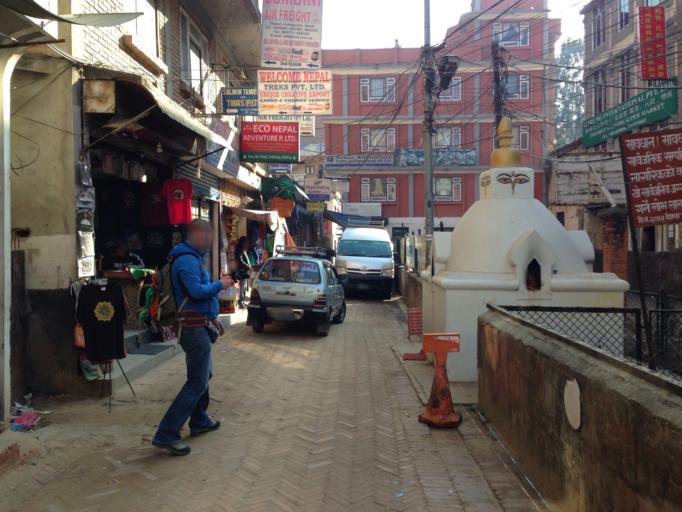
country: NP
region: Central Region
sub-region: Bagmati Zone
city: Kathmandu
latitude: 27.7132
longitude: 85.3110
